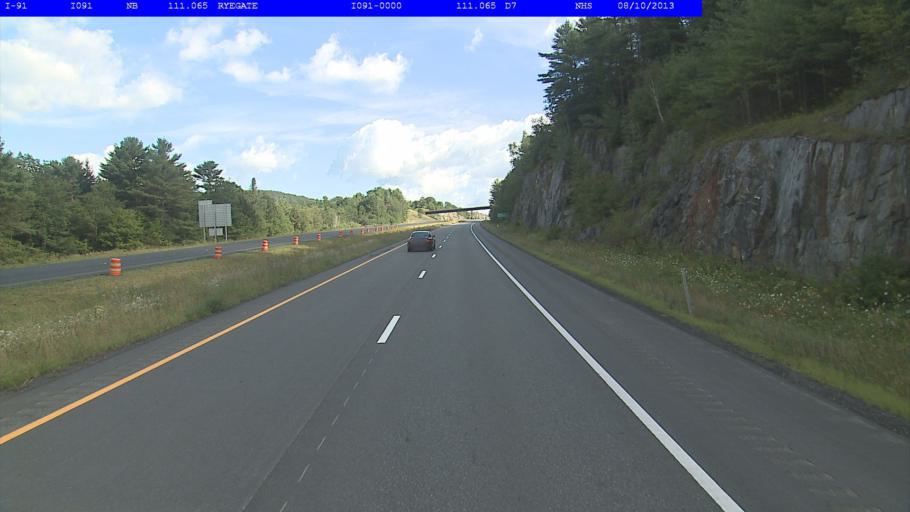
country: US
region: New Hampshire
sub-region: Grafton County
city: Woodsville
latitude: 44.1695
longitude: -72.0828
